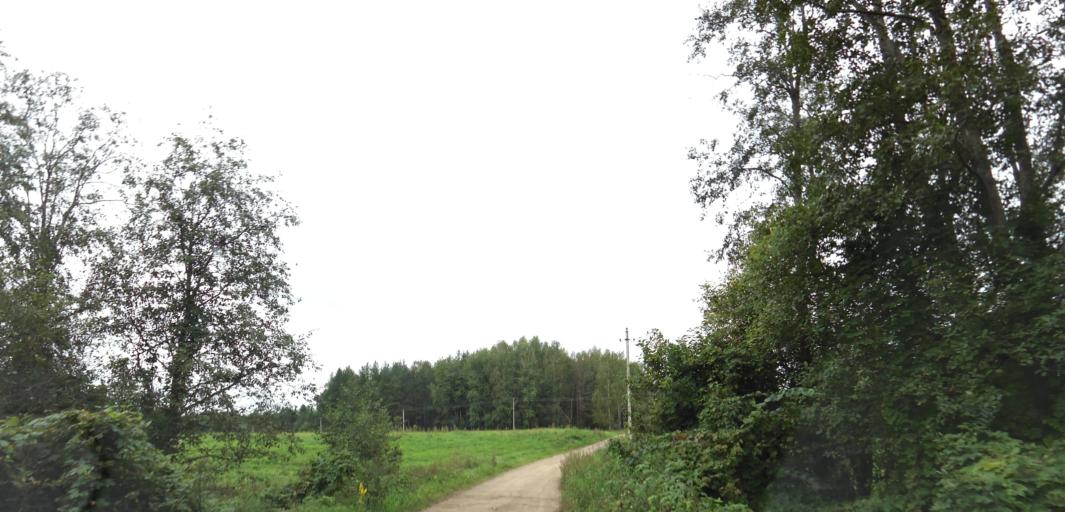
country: LT
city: Moletai
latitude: 55.3354
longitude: 25.3764
